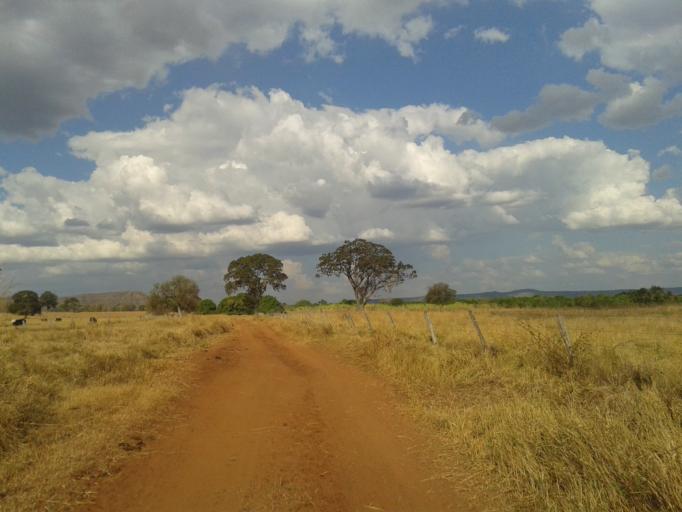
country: BR
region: Minas Gerais
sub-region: Santa Vitoria
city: Santa Vitoria
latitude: -19.1619
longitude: -50.0178
